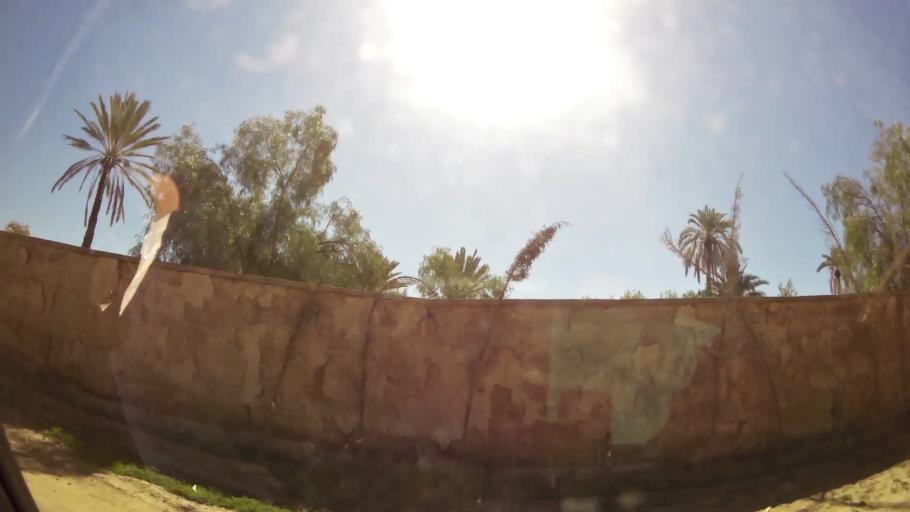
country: MA
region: Marrakech-Tensift-Al Haouz
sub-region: Marrakech
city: Marrakesh
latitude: 31.6701
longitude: -7.9599
